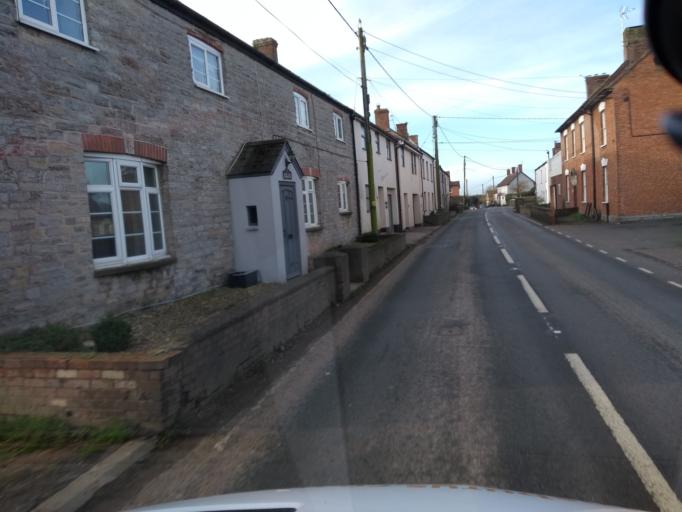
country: GB
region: England
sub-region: Somerset
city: Westonzoyland
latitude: 51.0561
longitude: -2.9507
